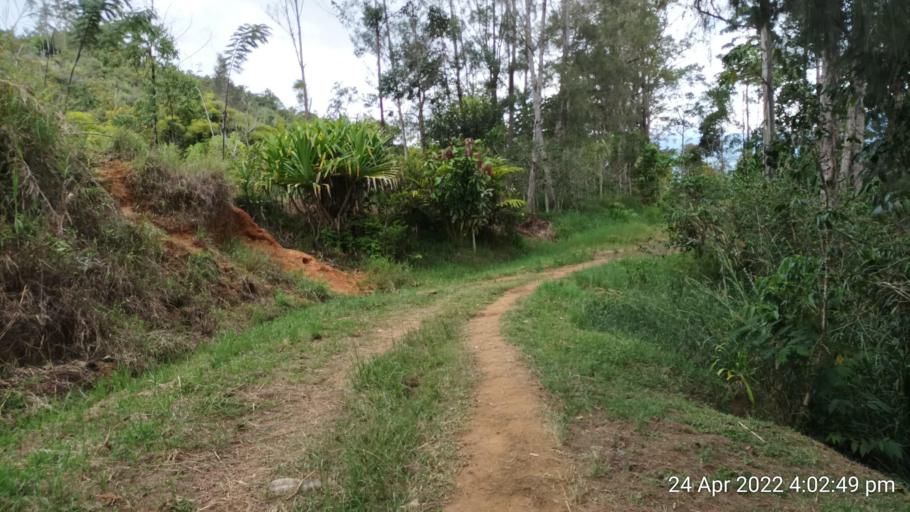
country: PG
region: Jiwaka
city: Minj
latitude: -5.9010
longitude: 144.8230
